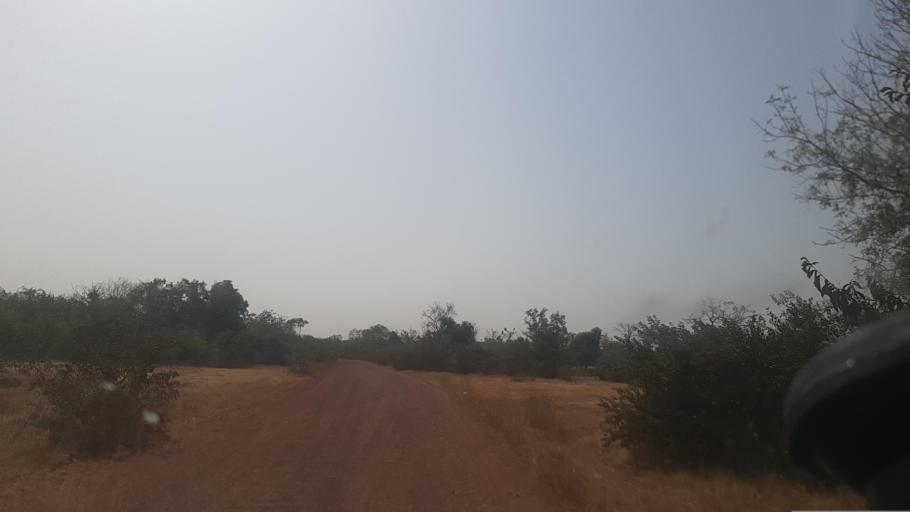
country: ML
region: Segou
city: Baroueli
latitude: 13.0703
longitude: -6.4799
